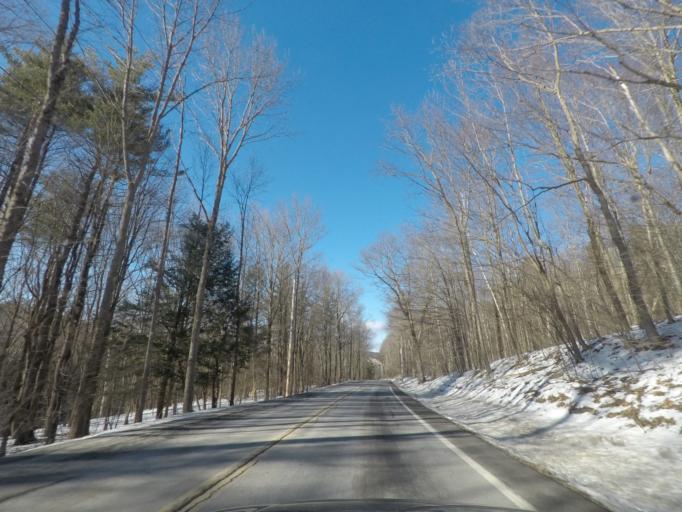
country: US
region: New York
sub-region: Columbia County
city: Chatham
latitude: 42.3497
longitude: -73.4817
